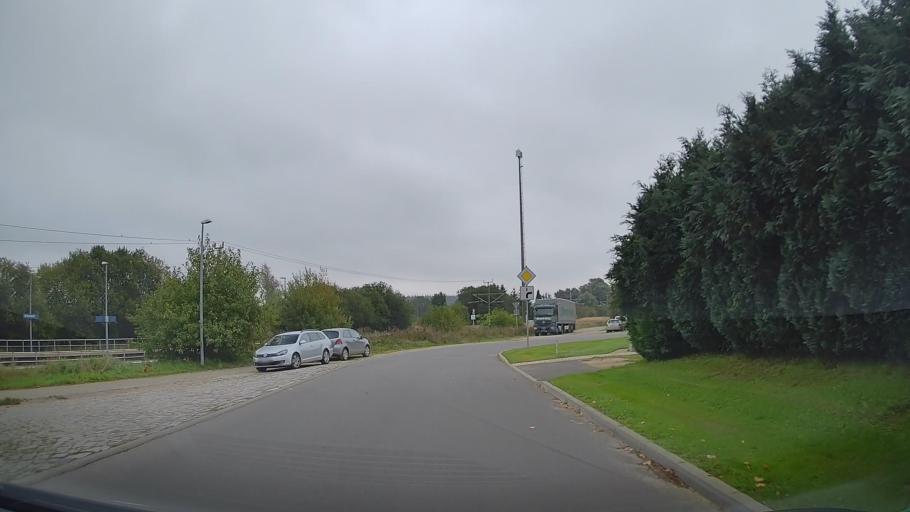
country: DE
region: Mecklenburg-Vorpommern
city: Dummerstorf
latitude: 53.9694
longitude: 12.2462
